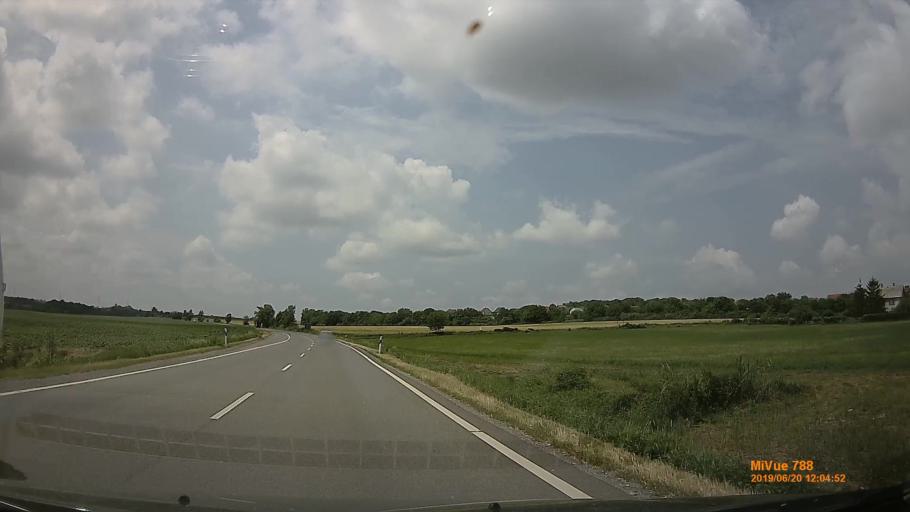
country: HU
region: Baranya
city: Pecsvarad
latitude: 46.1517
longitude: 18.4177
